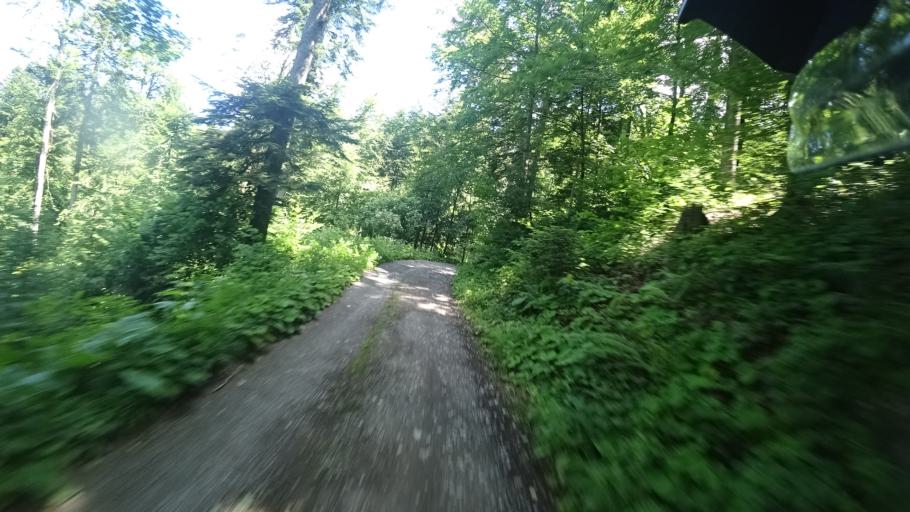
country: HR
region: Primorsko-Goranska
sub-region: Grad Delnice
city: Delnice
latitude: 45.4444
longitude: 14.7416
